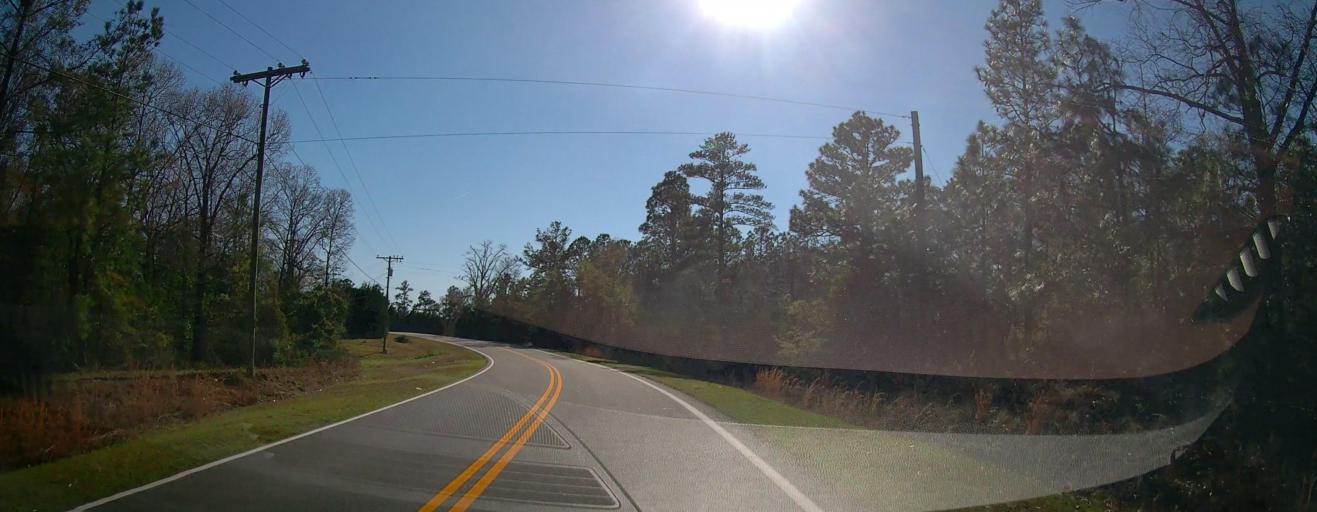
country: US
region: Georgia
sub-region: Peach County
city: Byron
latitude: 32.6881
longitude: -83.8035
